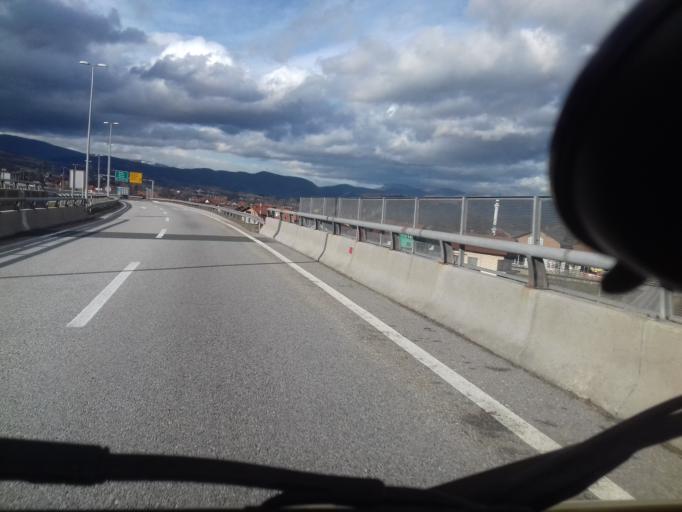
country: BA
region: Federation of Bosnia and Herzegovina
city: Visoko
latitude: 44.0046
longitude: 18.1741
